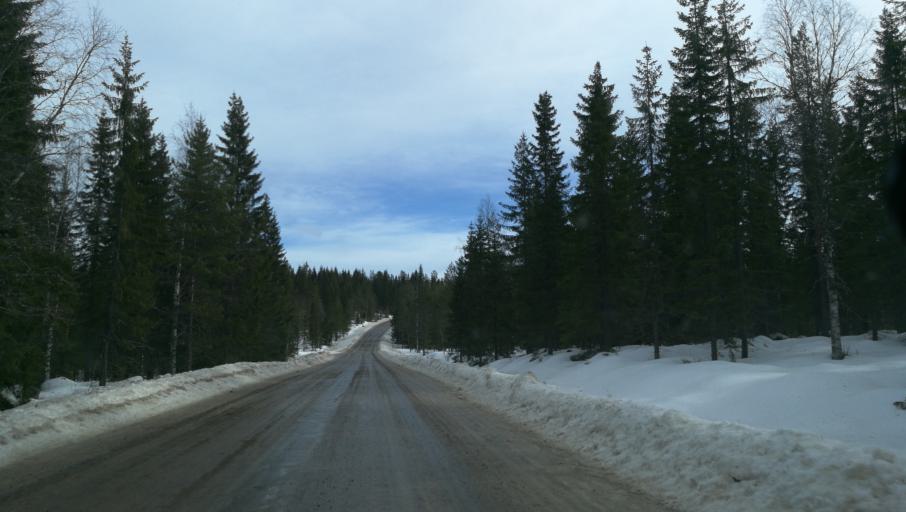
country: SE
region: Vaermland
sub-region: Torsby Kommun
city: Torsby
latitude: 60.6487
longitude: 12.9199
